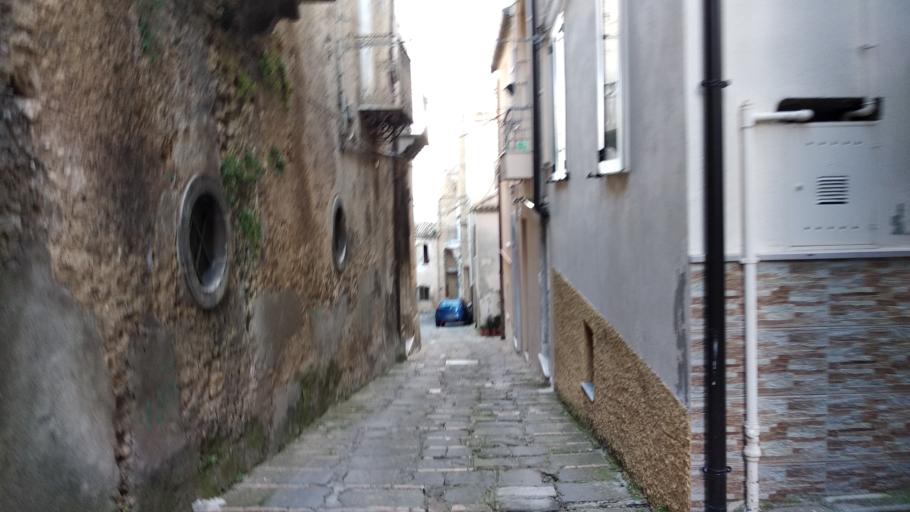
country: IT
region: Basilicate
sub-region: Provincia di Matera
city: Tricarico
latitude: 40.6250
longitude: 16.1434
